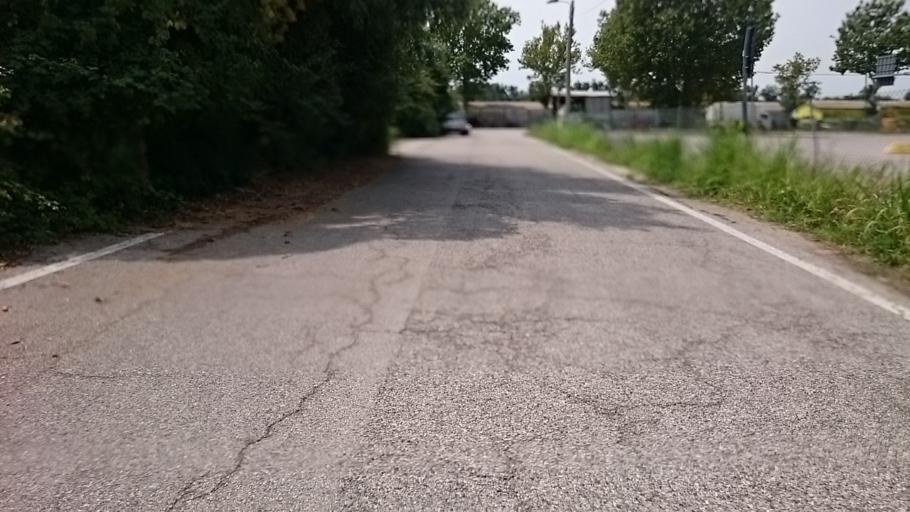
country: IT
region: Veneto
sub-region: Provincia di Venezia
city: Campalto
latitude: 45.4675
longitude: 12.2803
